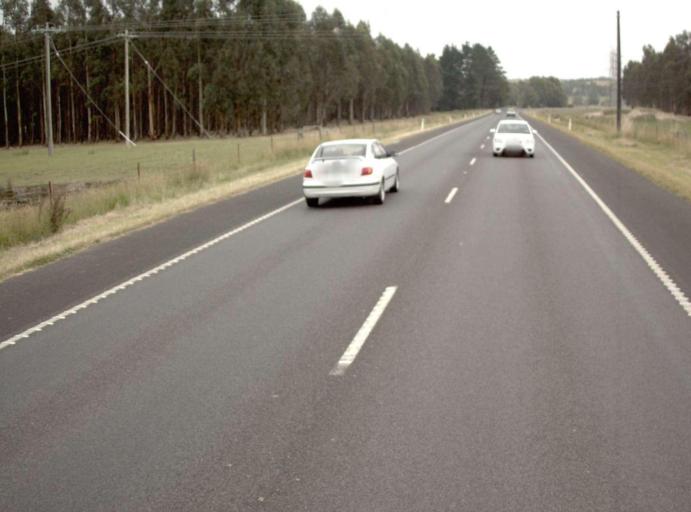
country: AU
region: Victoria
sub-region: Latrobe
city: Morwell
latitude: -38.2859
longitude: 146.4131
